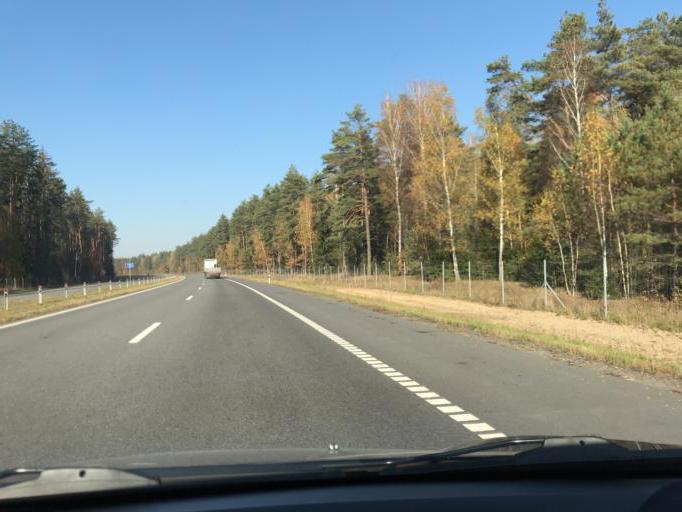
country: BY
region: Mogilev
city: Kirawsk
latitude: 53.2237
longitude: 29.3384
